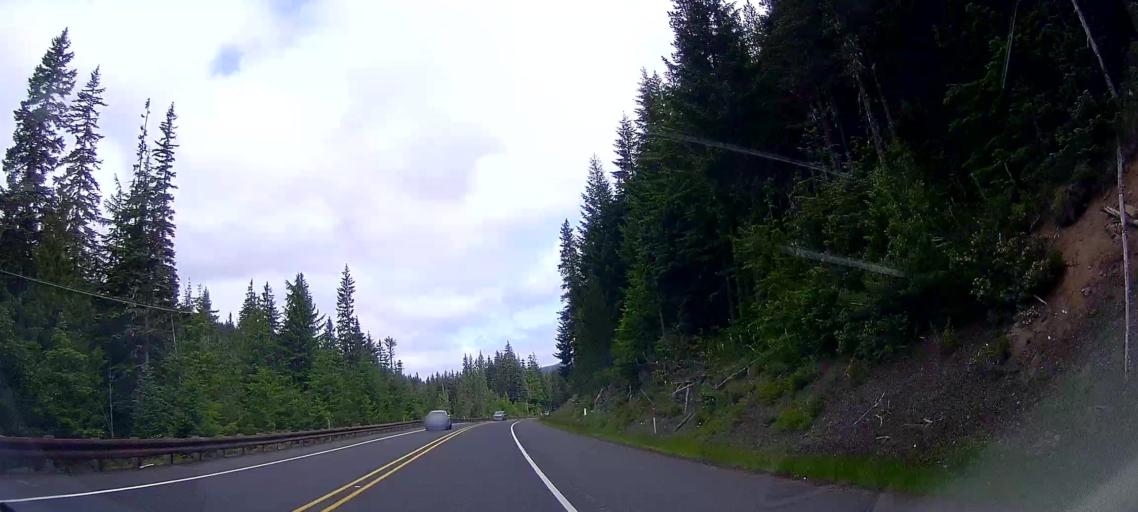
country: US
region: Oregon
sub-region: Clackamas County
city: Mount Hood Village
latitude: 45.2669
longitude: -121.7175
